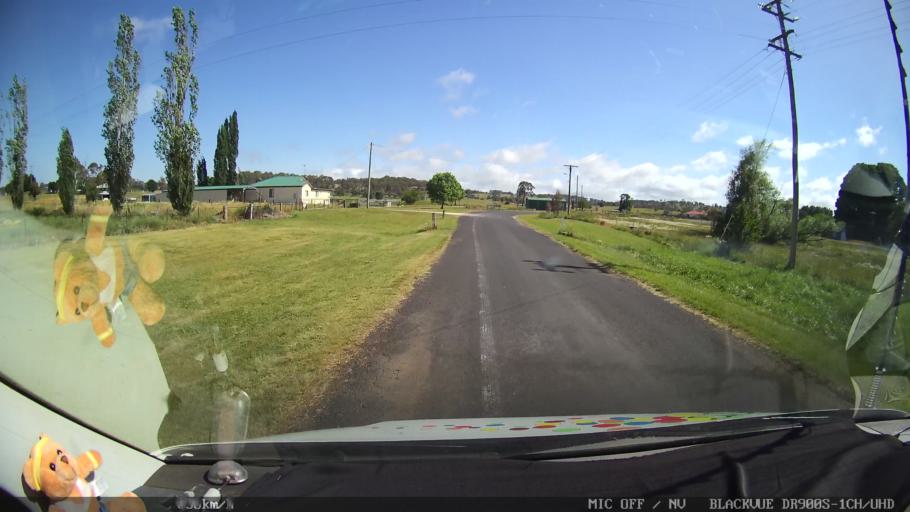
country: AU
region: New South Wales
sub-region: Guyra
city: Guyra
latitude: -30.1298
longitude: 151.6832
